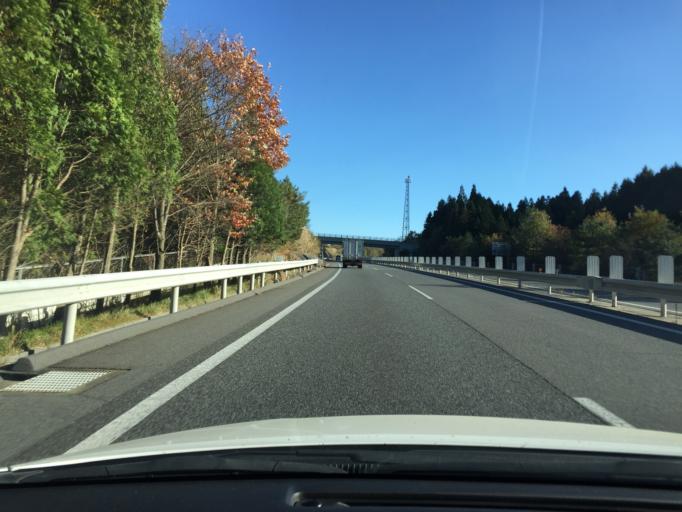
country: JP
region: Fukushima
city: Ishikawa
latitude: 37.2238
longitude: 140.6861
